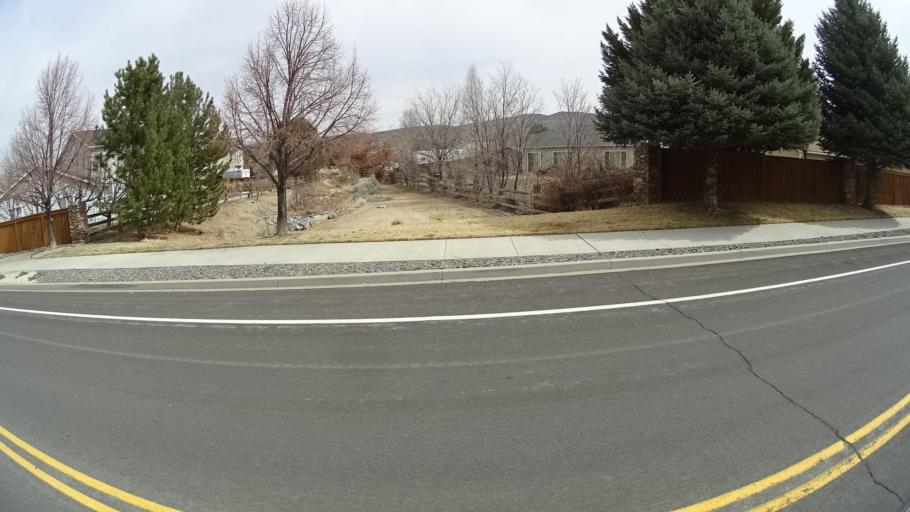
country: US
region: Nevada
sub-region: Washoe County
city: Spanish Springs
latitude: 39.6301
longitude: -119.6847
